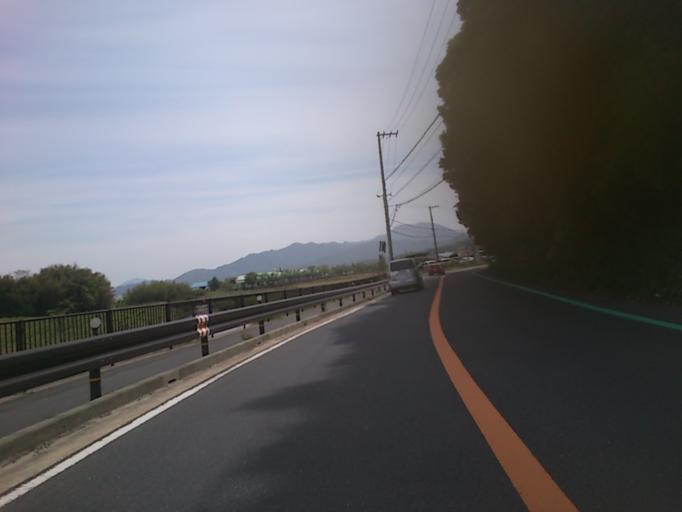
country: JP
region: Kyoto
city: Miyazu
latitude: 35.6363
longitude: 135.0802
